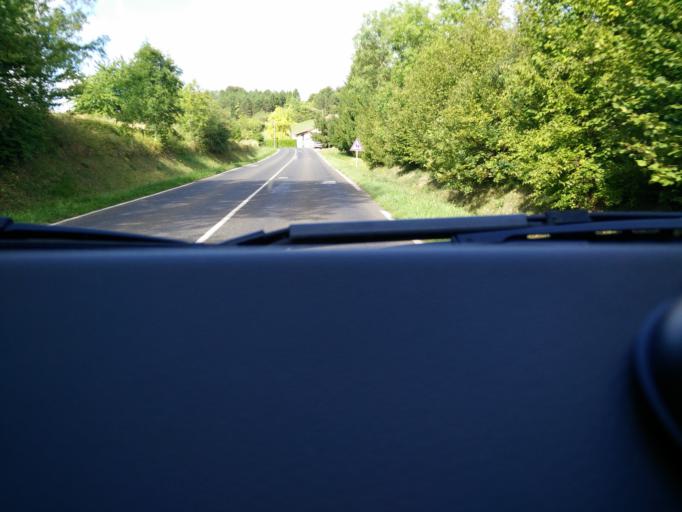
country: FR
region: Lorraine
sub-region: Departement de la Meuse
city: Etain
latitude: 49.1190
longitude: 5.5615
